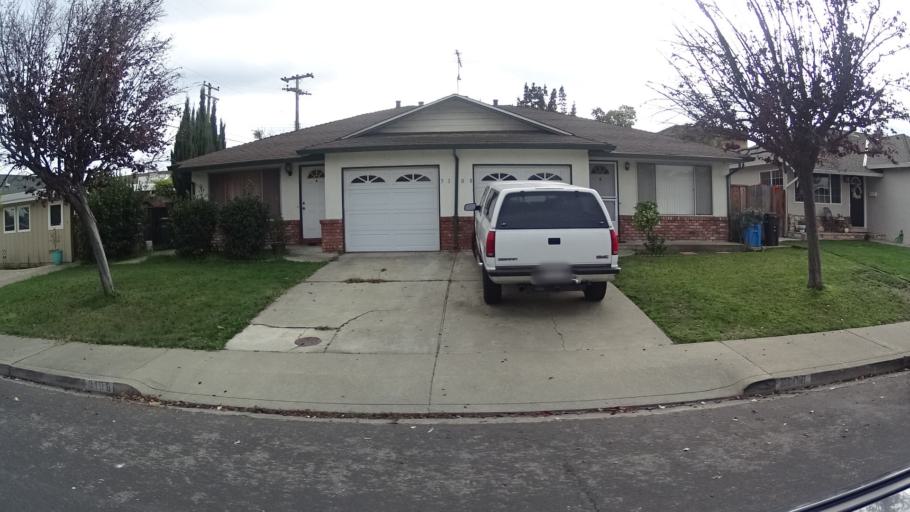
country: US
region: California
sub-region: Santa Clara County
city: Santa Clara
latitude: 37.3243
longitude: -121.9834
